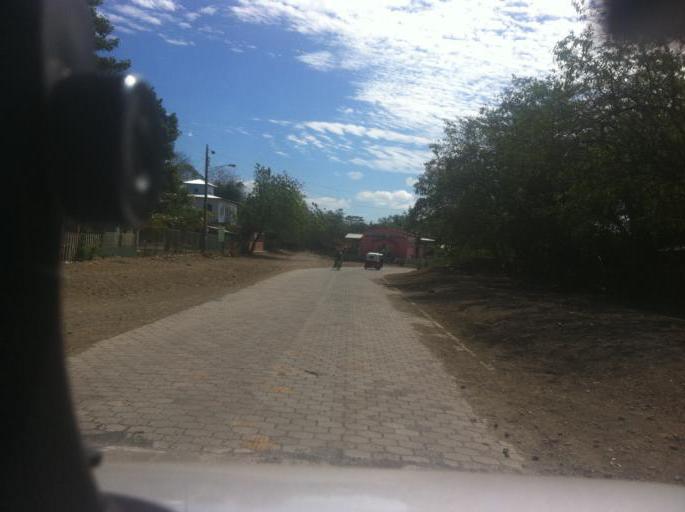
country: NI
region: Rivas
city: Tola
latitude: 11.5124
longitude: -86.0810
